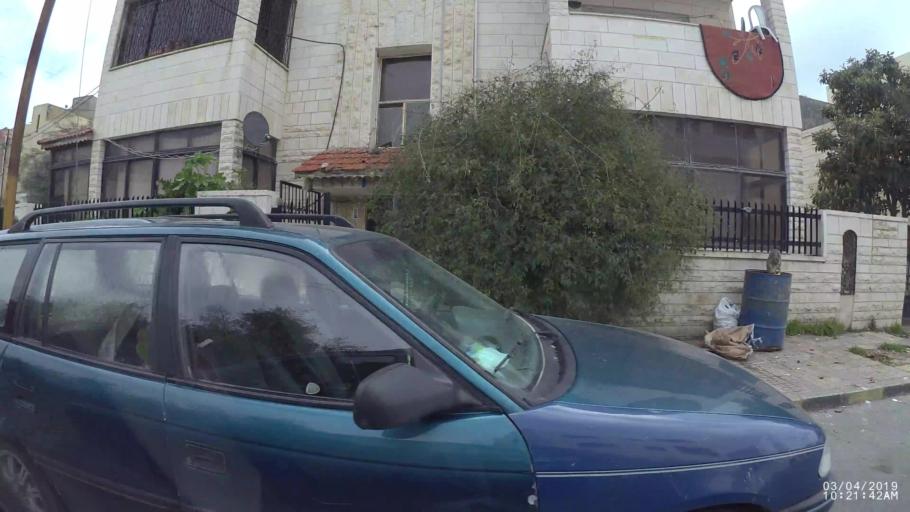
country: JO
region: Amman
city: Wadi as Sir
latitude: 31.9481
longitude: 35.8230
